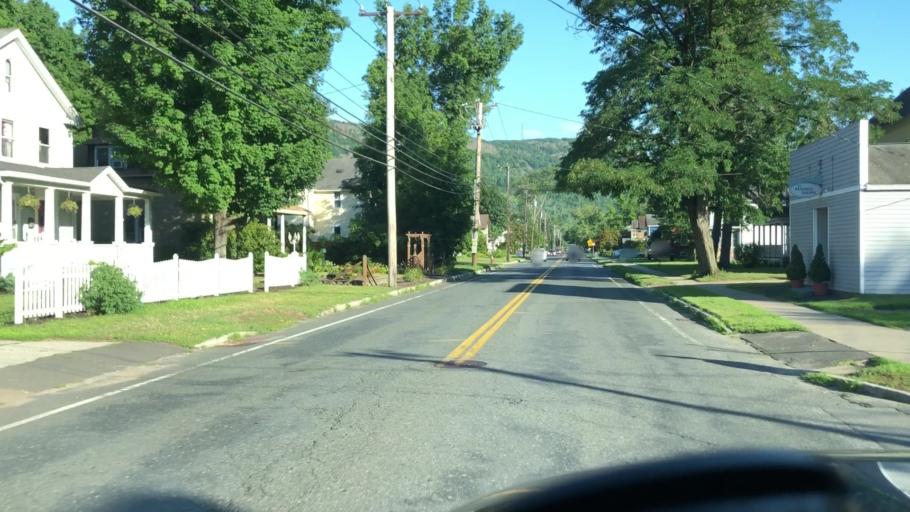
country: US
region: Massachusetts
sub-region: Hampshire County
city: Easthampton
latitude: 42.2615
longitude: -72.6619
